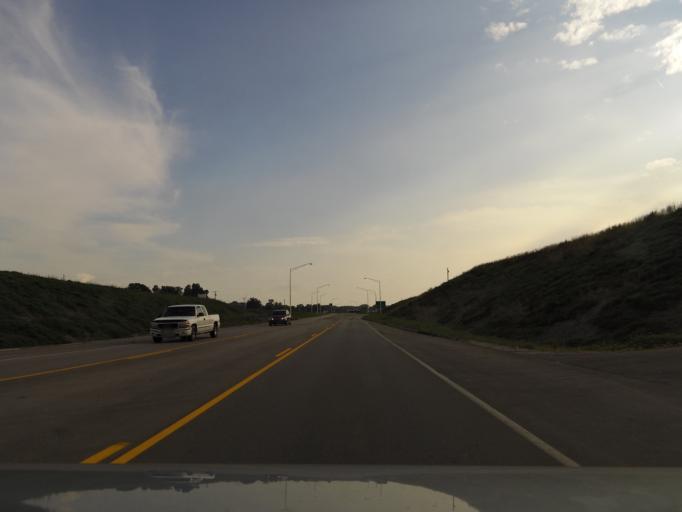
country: US
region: Kentucky
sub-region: Harrison County
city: Cynthiana
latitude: 38.3708
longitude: -84.3179
